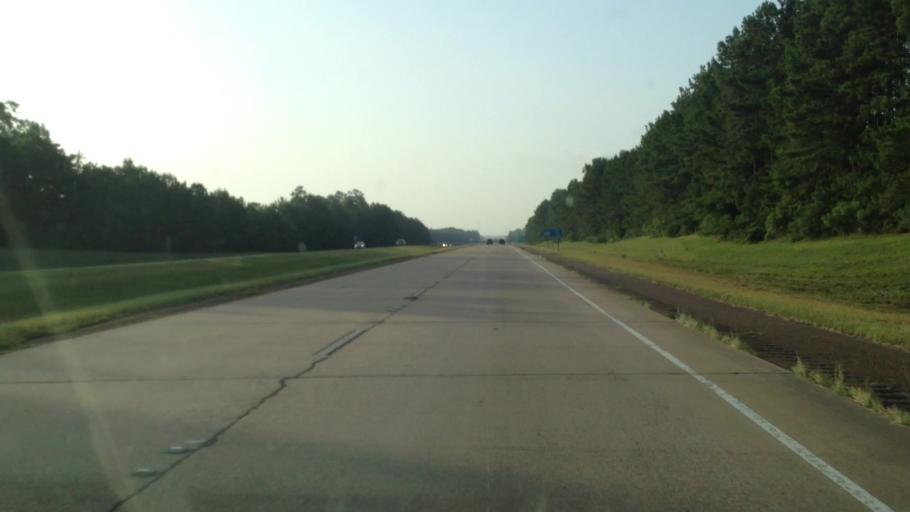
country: US
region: Louisiana
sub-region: Rapides Parish
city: Boyce
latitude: 31.4162
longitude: -92.7267
